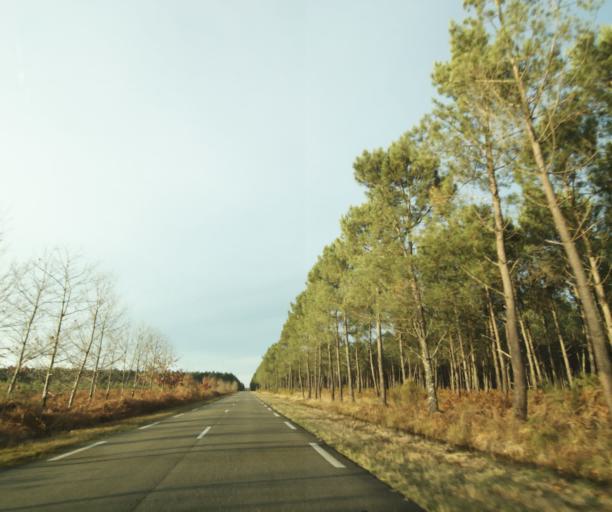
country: FR
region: Aquitaine
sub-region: Departement des Landes
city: Gabarret
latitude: 44.1341
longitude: -0.1163
